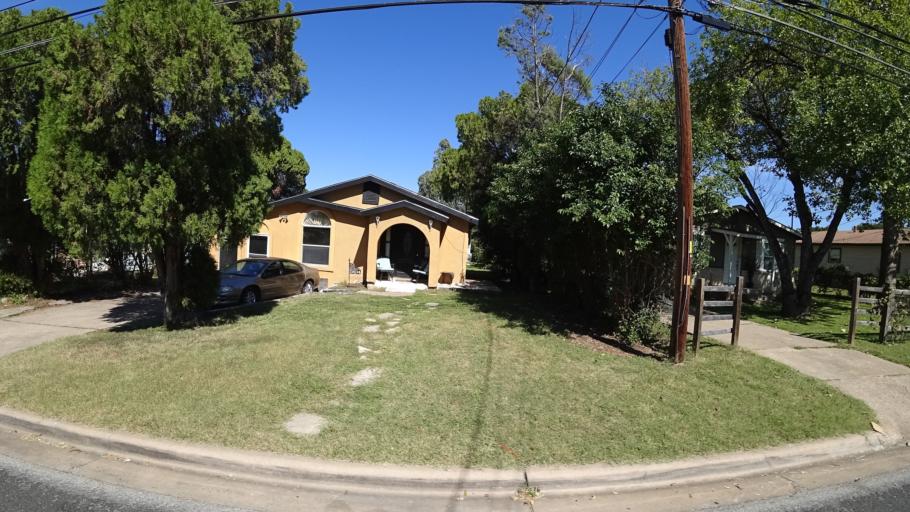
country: US
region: Texas
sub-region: Travis County
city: Austin
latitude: 30.2796
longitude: -97.6743
